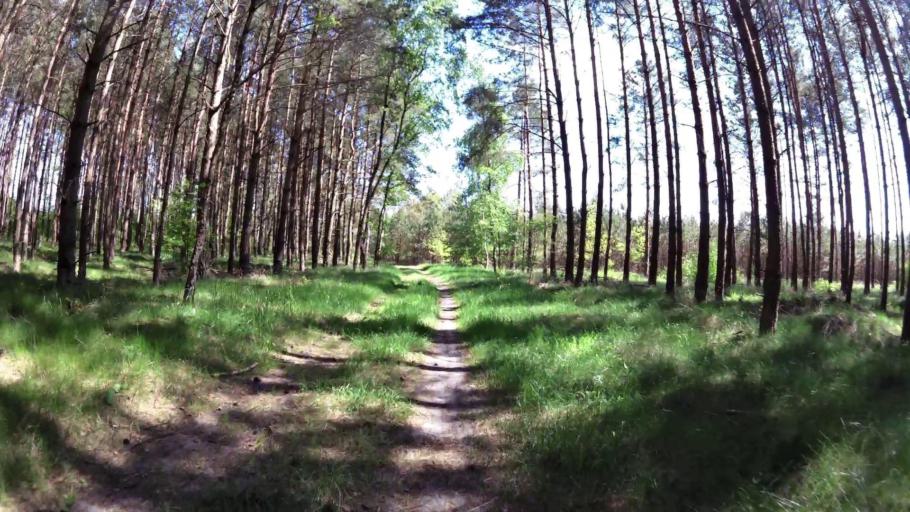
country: PL
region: West Pomeranian Voivodeship
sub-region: Powiat bialogardzki
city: Bialogard
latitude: 53.9947
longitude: 16.0401
